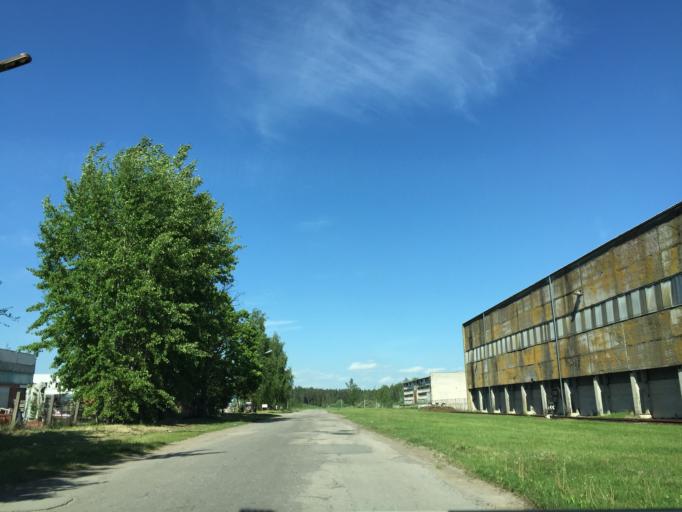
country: LV
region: Ozolnieku
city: Ozolnieki
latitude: 56.6651
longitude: 23.8010
